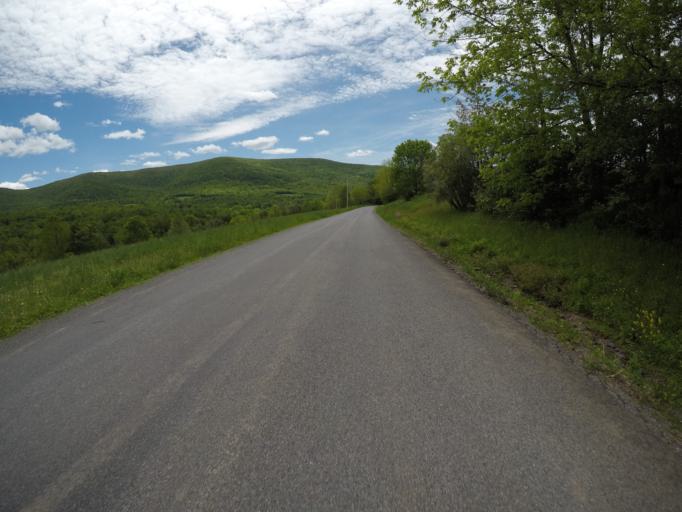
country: US
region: New York
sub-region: Delaware County
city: Stamford
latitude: 42.2680
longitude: -74.5189
